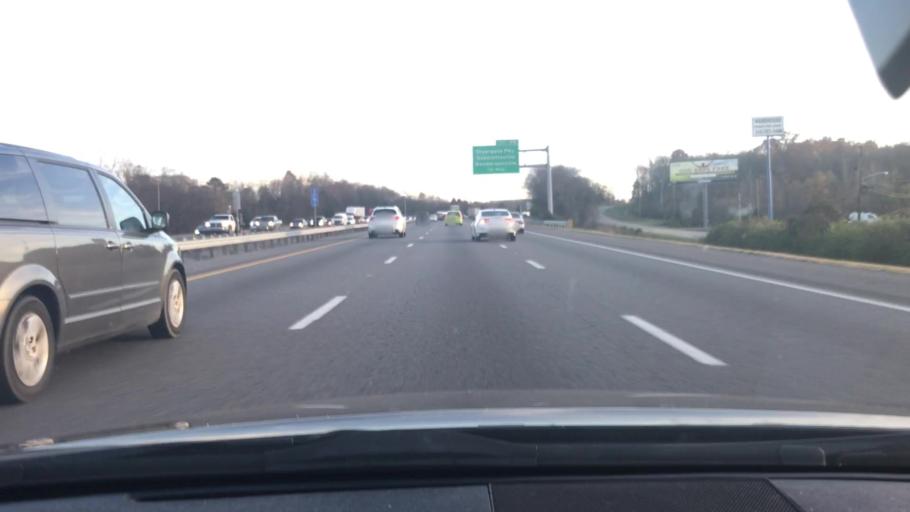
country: US
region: Tennessee
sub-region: Davidson County
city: Goodlettsville
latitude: 36.3192
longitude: -86.7029
